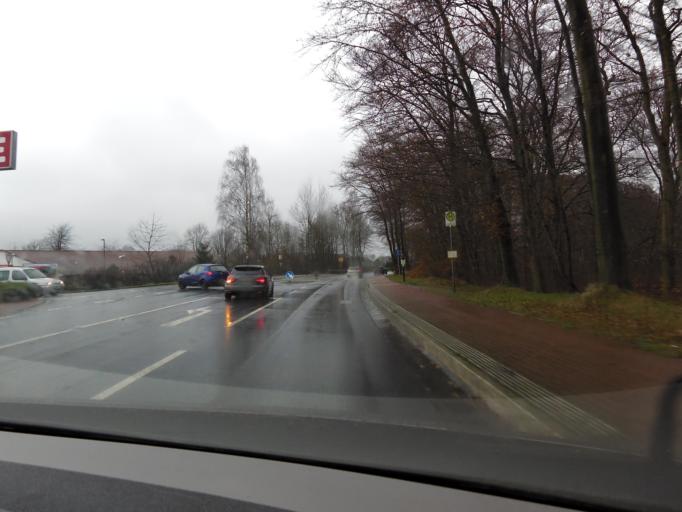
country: DE
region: Lower Saxony
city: Bad Fallingbostel
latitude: 52.8727
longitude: 9.7004
